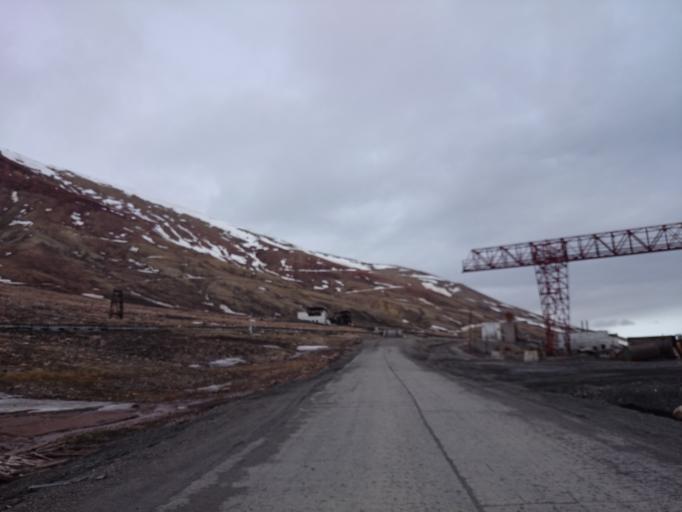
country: SJ
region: Svalbard
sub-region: Spitsbergen
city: Longyearbyen
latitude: 78.6548
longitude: 16.3519
